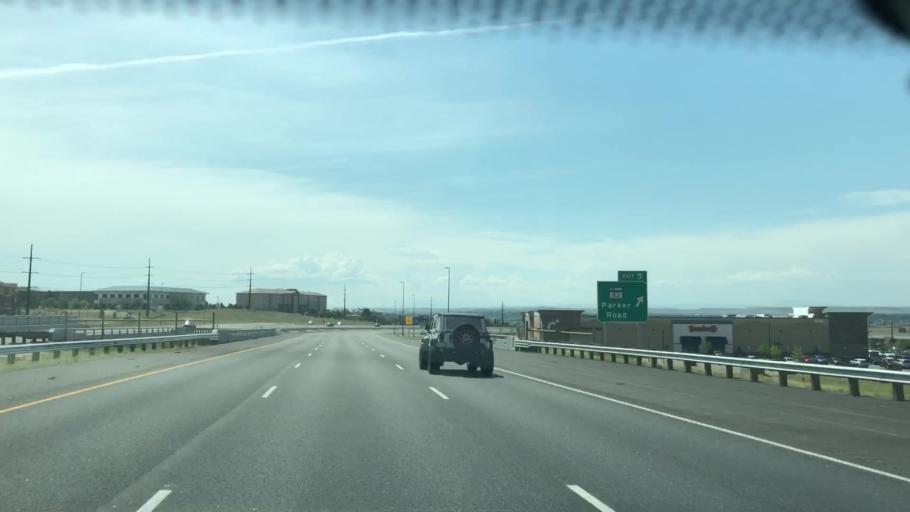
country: US
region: Colorado
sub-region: Douglas County
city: Parker
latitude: 39.5586
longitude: -104.7710
